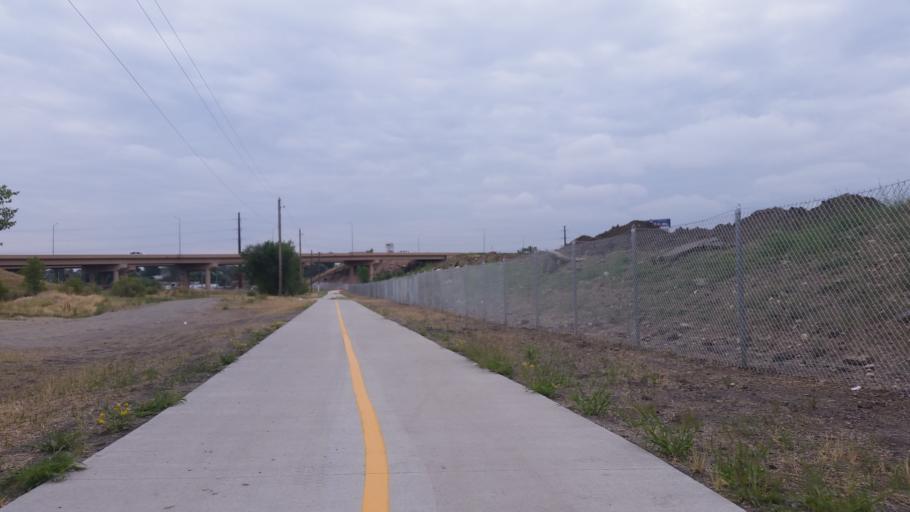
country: US
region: Colorado
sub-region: Adams County
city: Berkley
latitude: 39.8078
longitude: -105.0158
